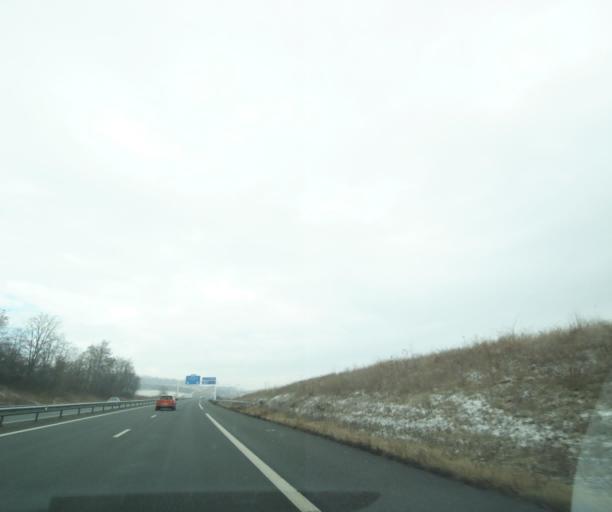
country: FR
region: Auvergne
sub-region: Departement du Puy-de-Dome
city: Combronde
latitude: 45.9584
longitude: 3.1029
